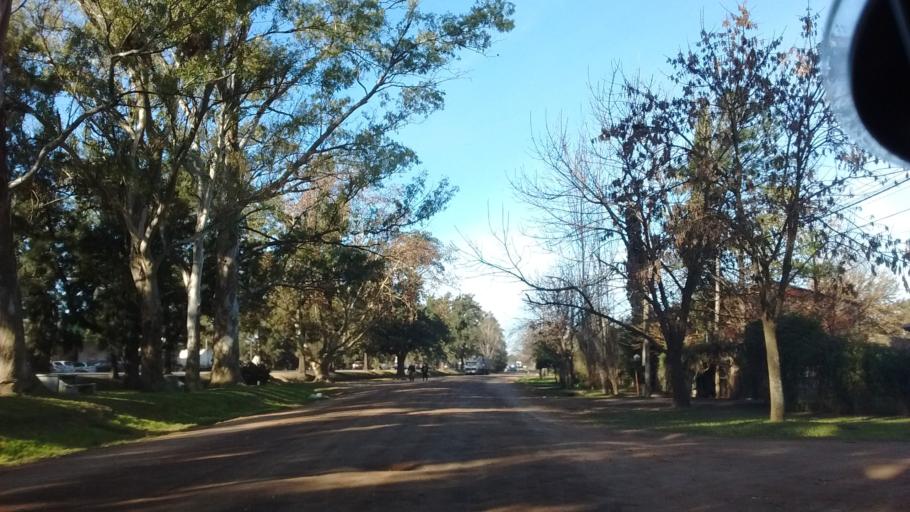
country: AR
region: Santa Fe
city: Funes
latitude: -32.9231
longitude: -60.8030
